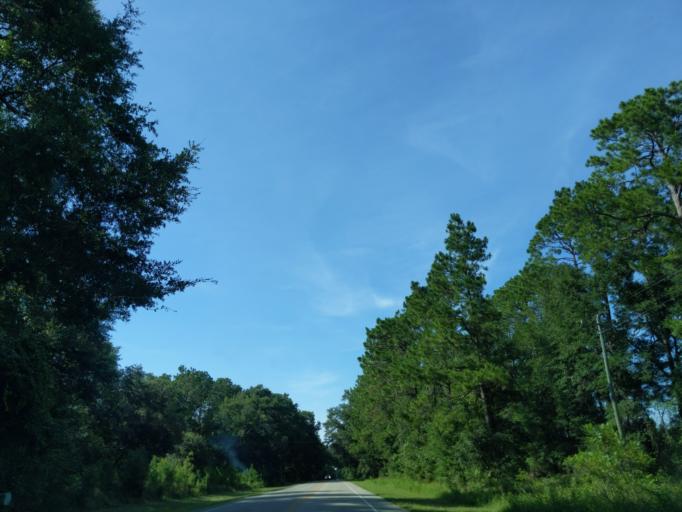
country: US
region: Florida
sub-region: Leon County
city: Woodville
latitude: 30.2920
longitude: -84.3121
